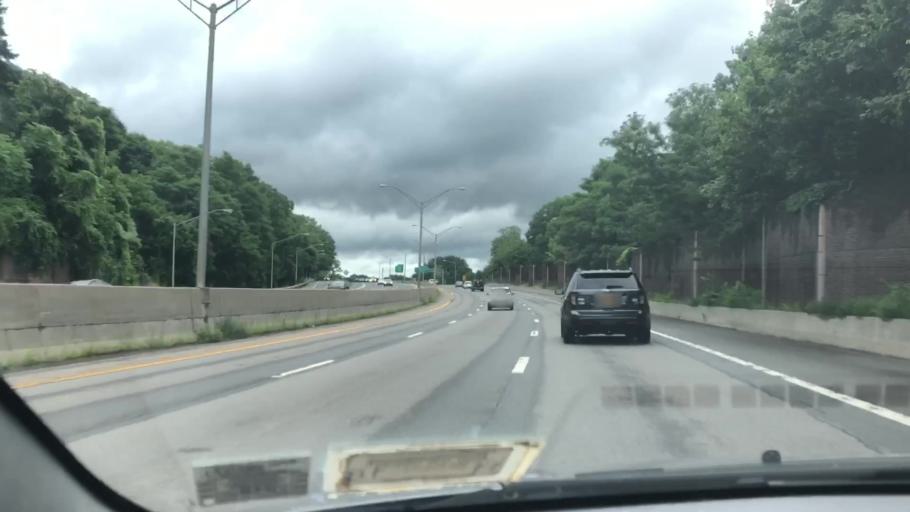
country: US
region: New York
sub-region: Monroe County
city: Pittsford
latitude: 43.1199
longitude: -77.5166
